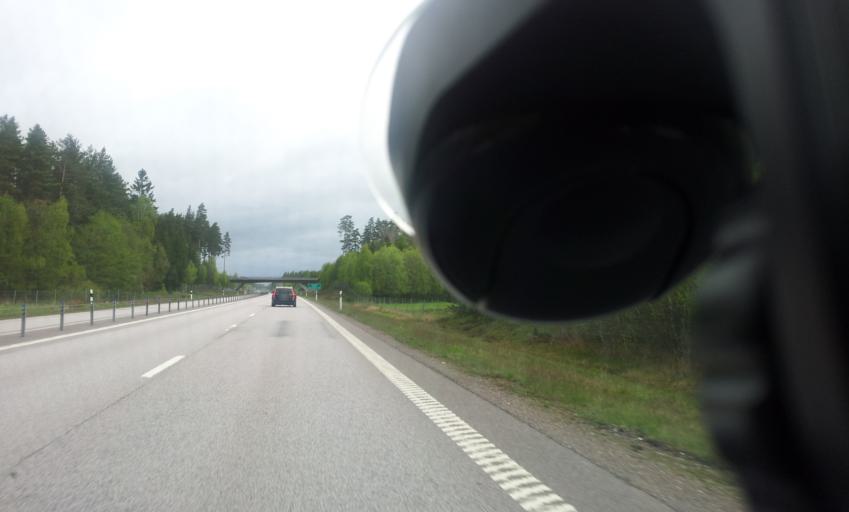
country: SE
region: Kalmar
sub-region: Torsas Kommun
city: Torsas
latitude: 56.5081
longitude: 16.0868
